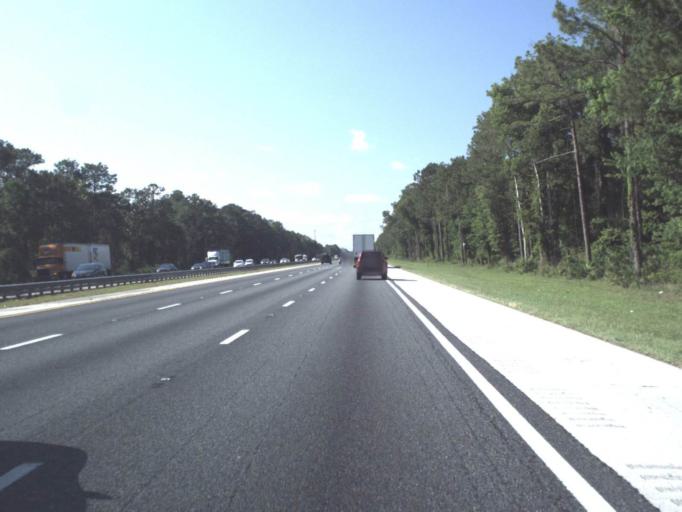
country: US
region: Florida
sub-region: Saint Johns County
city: Saint Augustine
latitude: 29.8781
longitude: -81.4002
